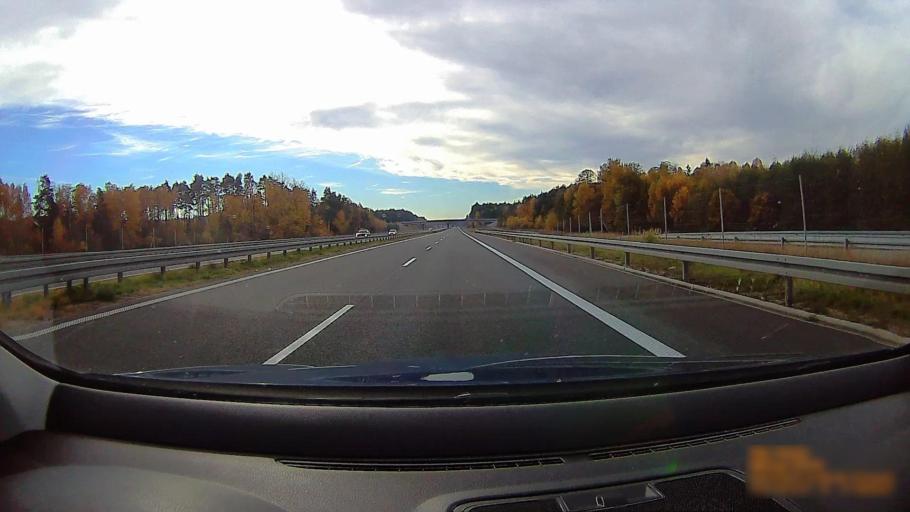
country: PL
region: Greater Poland Voivodeship
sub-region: Powiat ostrowski
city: Przygodzice
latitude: 51.5697
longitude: 17.8481
